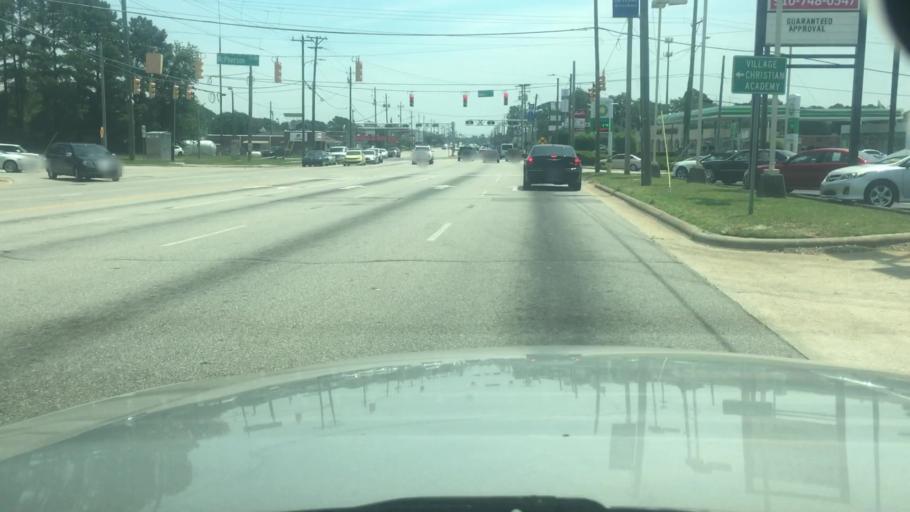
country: US
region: North Carolina
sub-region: Cumberland County
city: Fayetteville
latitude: 35.0442
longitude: -78.9356
